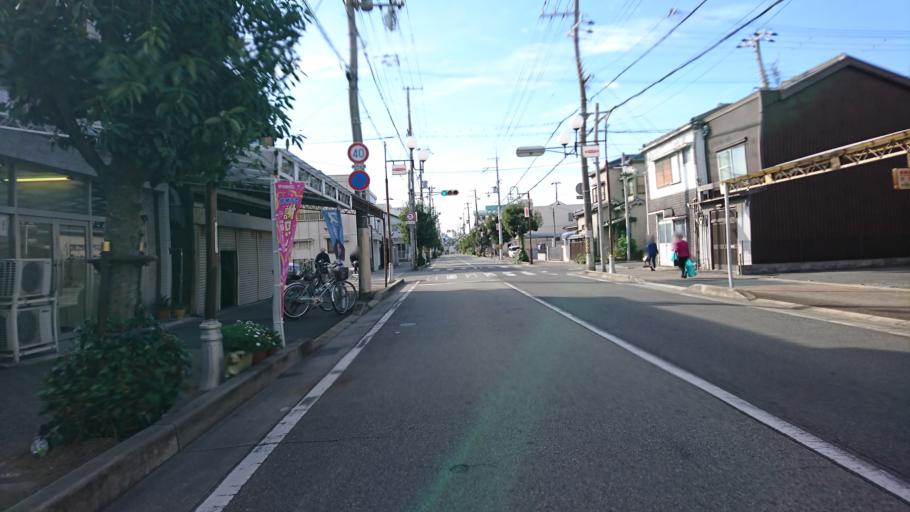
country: JP
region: Hyogo
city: Kakogawacho-honmachi
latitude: 34.7464
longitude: 134.8026
